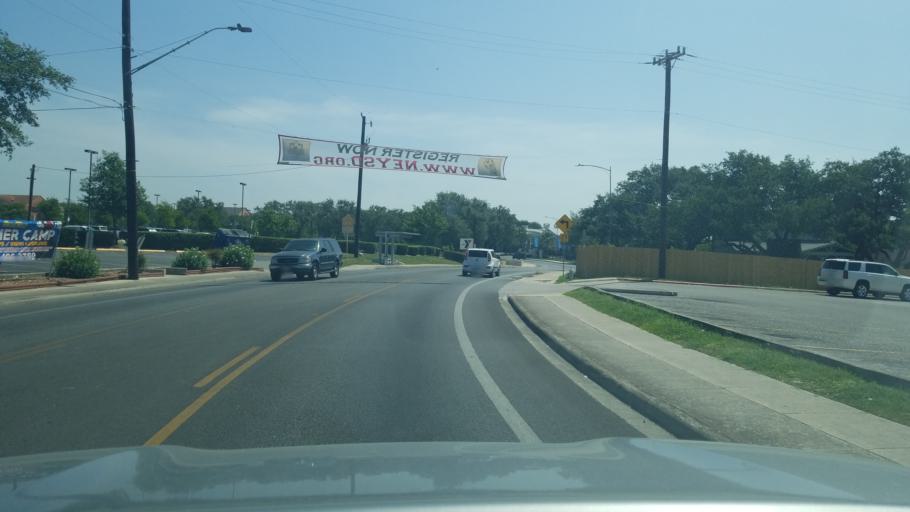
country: US
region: Texas
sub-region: Bexar County
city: Hollywood Park
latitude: 29.5882
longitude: -98.4501
